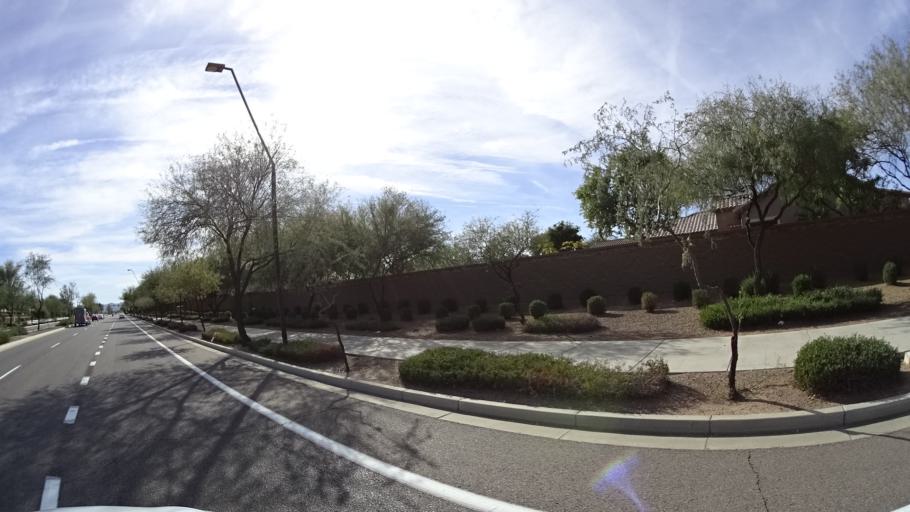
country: US
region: Arizona
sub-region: Maricopa County
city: Queen Creek
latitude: 33.2552
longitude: -111.6860
